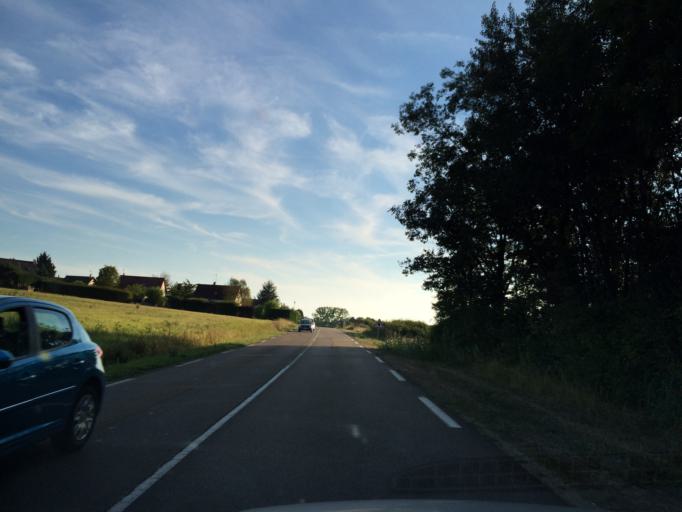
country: FR
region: Bourgogne
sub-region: Departement de l'Yonne
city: Saint-Georges-sur-Baulche
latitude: 47.8322
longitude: 3.5457
